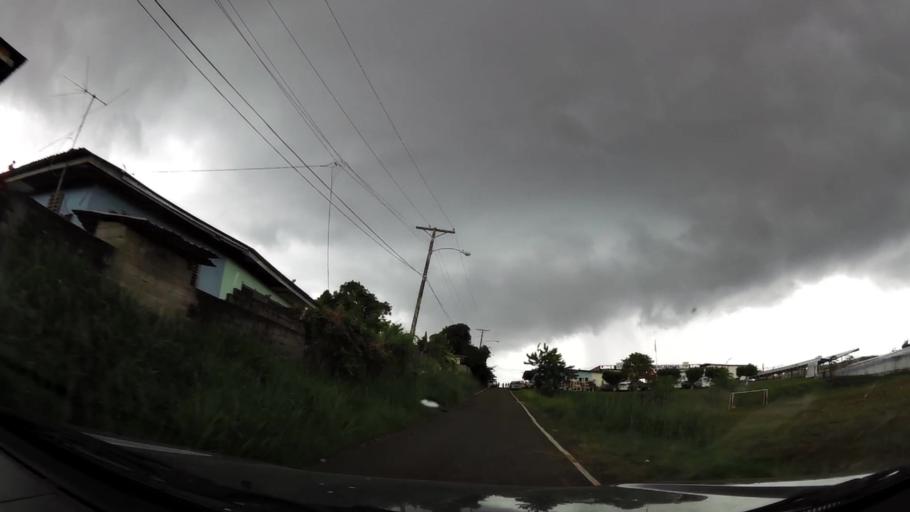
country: PA
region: Panama
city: San Miguelito
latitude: 9.0541
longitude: -79.4423
